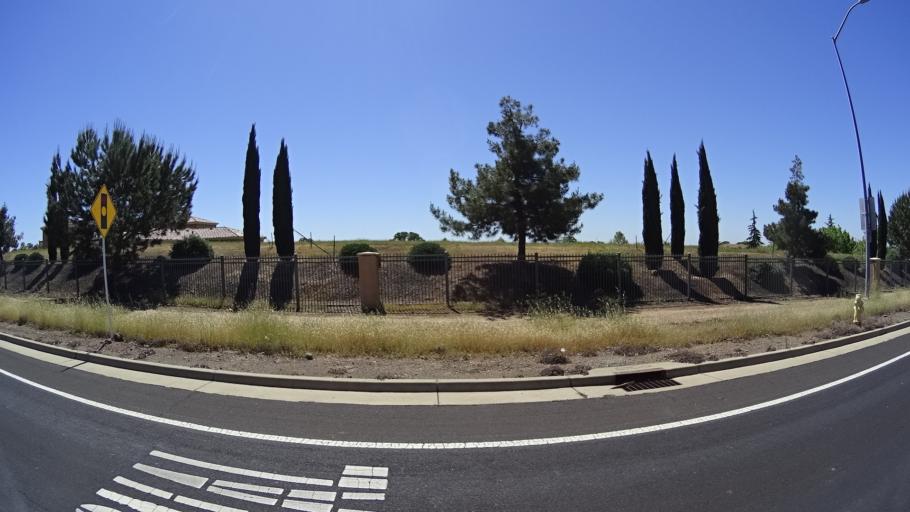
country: US
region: California
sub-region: Placer County
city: Rocklin
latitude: 38.7695
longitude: -121.2194
